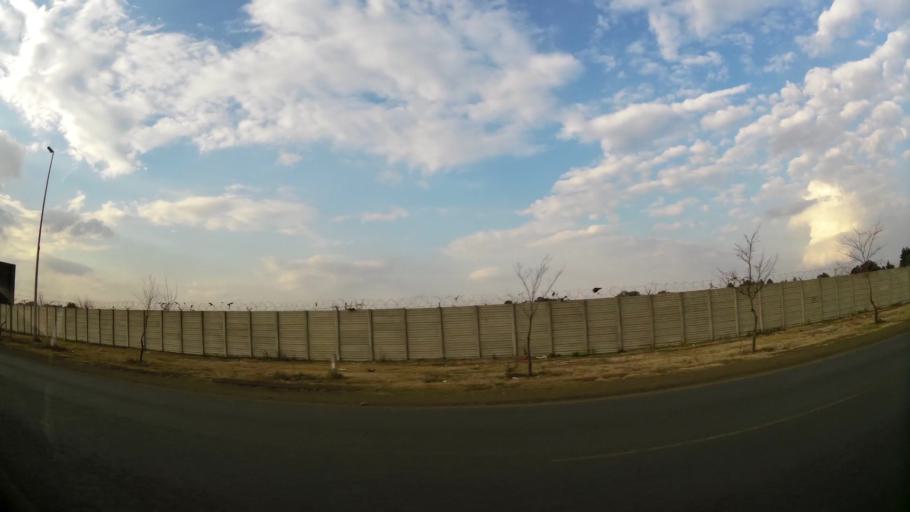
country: ZA
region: Gauteng
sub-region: Sedibeng District Municipality
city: Vanderbijlpark
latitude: -26.6935
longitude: 27.8056
